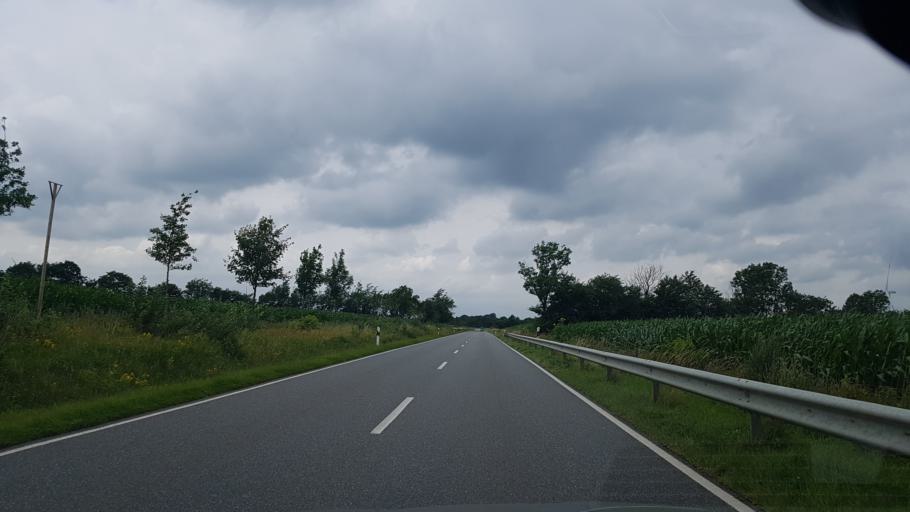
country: DE
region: Schleswig-Holstein
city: Boxlund
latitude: 54.8531
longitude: 9.1845
